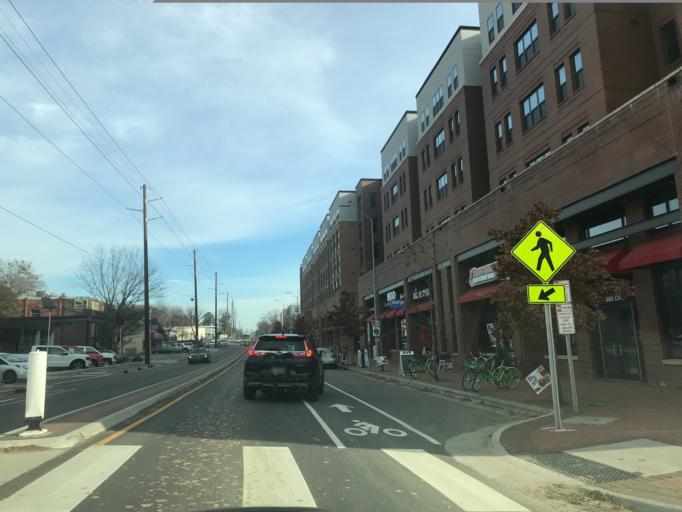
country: US
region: North Carolina
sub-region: Wake County
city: West Raleigh
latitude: 35.7899
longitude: -78.6777
